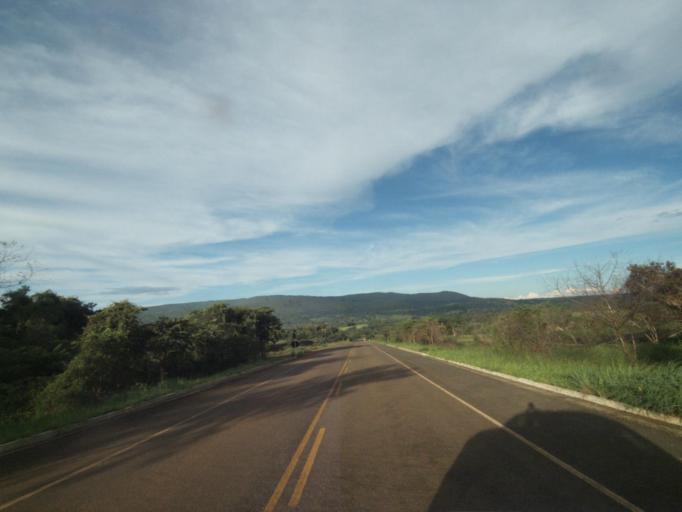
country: BR
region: Goias
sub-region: Jaragua
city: Jaragua
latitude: -15.8474
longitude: -49.3699
